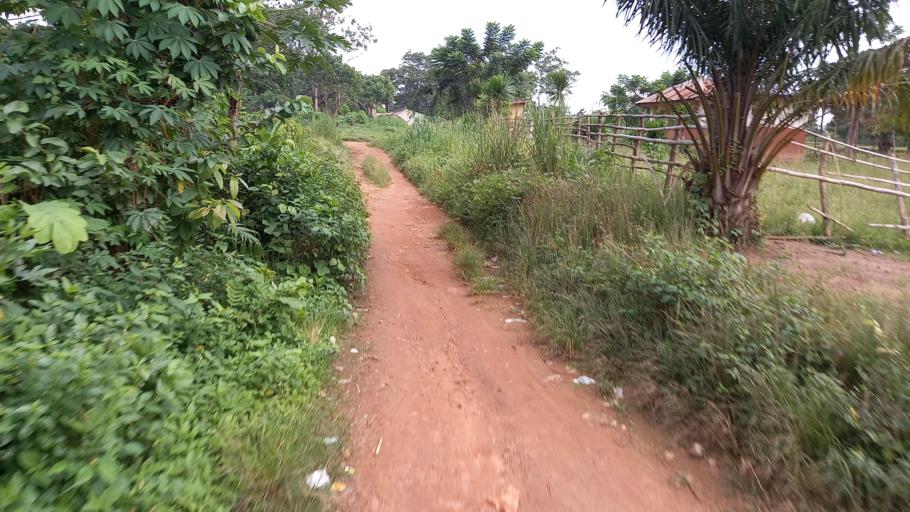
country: SL
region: Eastern Province
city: Kailahun
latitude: 8.2842
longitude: -10.5749
